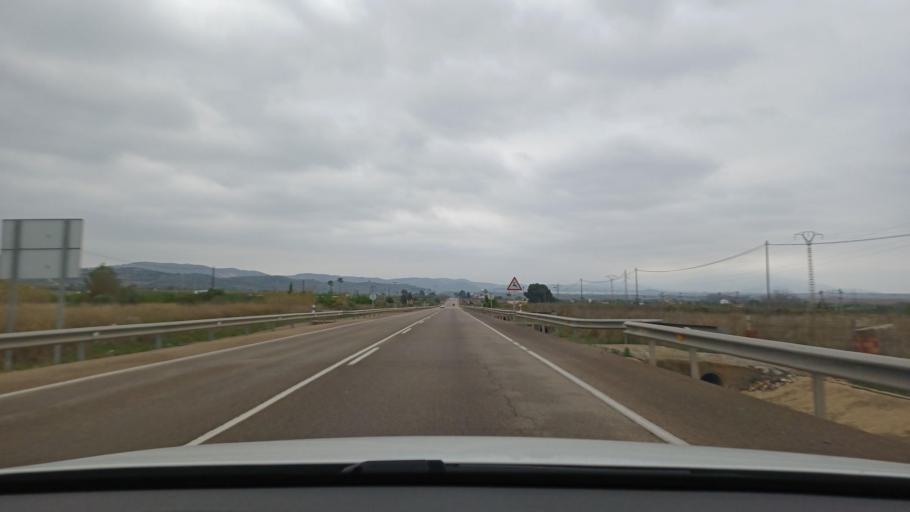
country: ES
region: Valencia
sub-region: Provincia de Castello
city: Torreblanca
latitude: 40.1655
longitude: 0.1650
